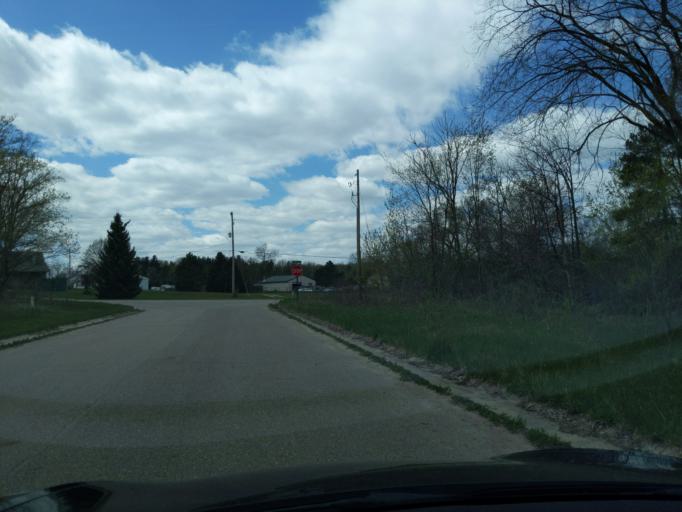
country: US
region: Michigan
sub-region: Eaton County
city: Dimondale
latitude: 42.6341
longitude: -84.6141
